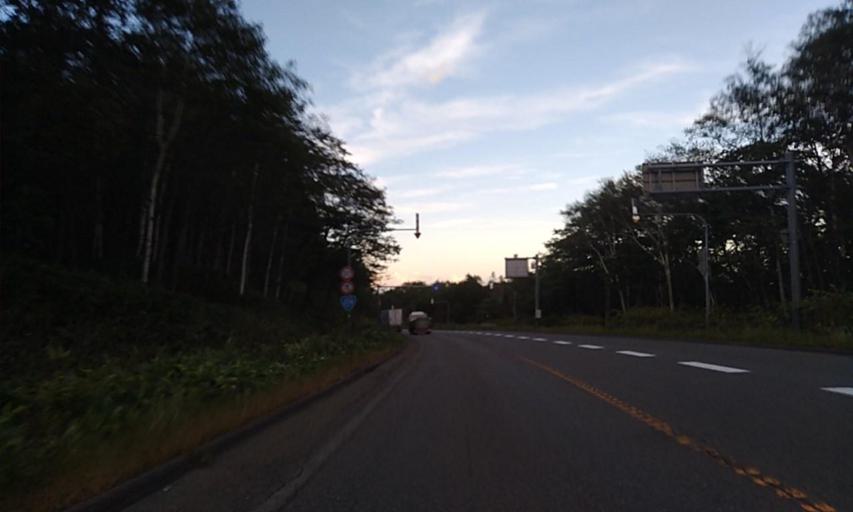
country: JP
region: Hokkaido
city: Otofuke
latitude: 42.9633
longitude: 142.7983
